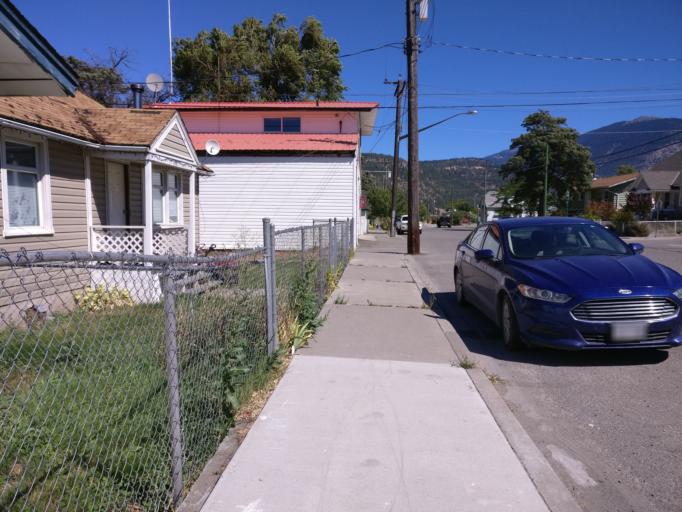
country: CA
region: British Columbia
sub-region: Thompson-Nicola Regional District
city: Ashcroft
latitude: 50.2318
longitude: -121.5825
